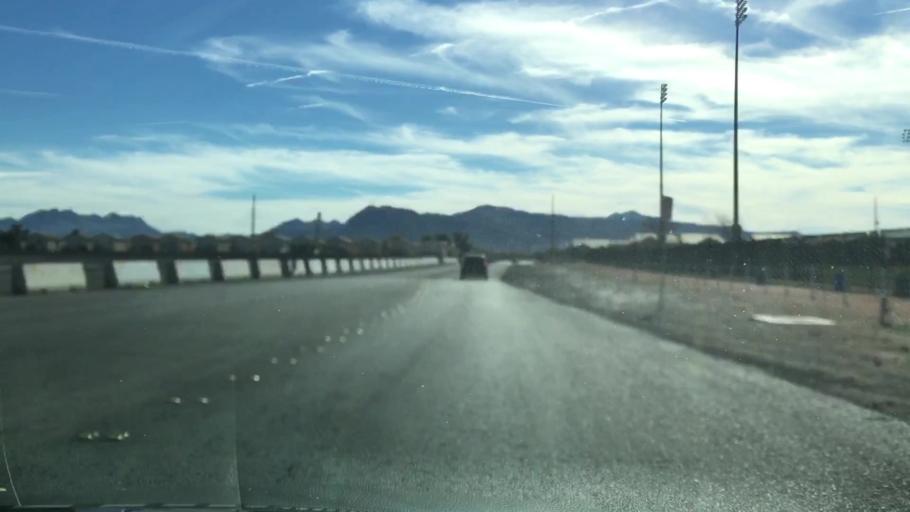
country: US
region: Nevada
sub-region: Clark County
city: Henderson
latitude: 36.0844
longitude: -115.0205
